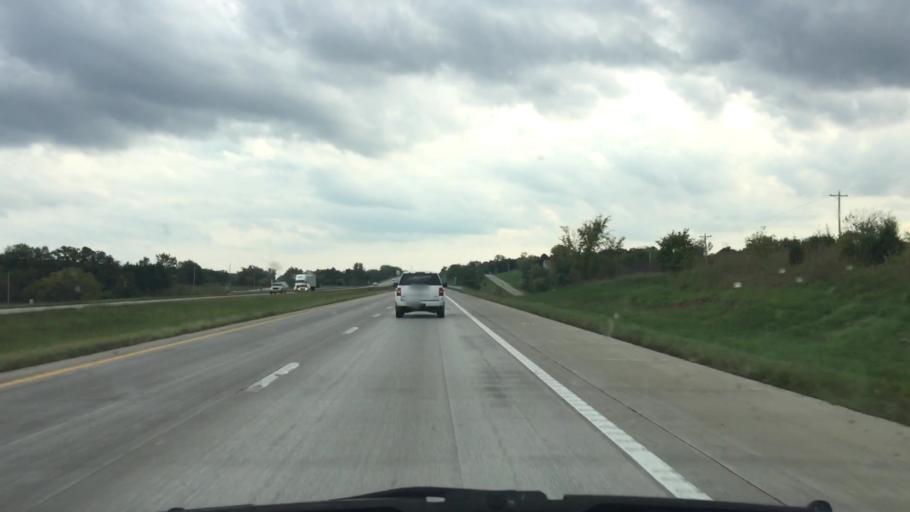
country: US
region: Missouri
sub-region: Clinton County
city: Cameron
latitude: 39.6607
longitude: -94.2376
